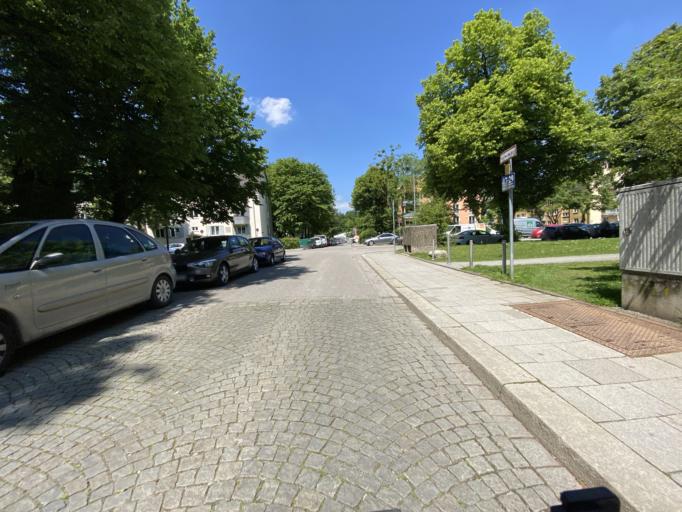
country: DE
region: Bavaria
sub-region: Upper Bavaria
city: Munich
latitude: 48.1202
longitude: 11.5270
